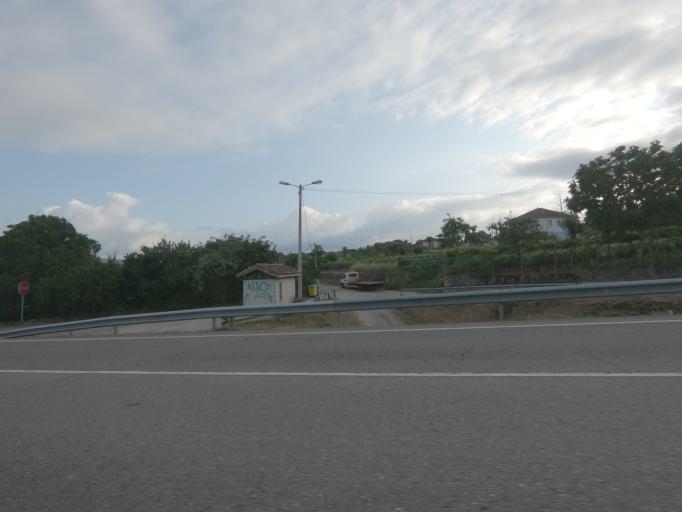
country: ES
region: Galicia
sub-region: Provincia de Ourense
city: Allariz
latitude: 42.2122
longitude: -7.8211
